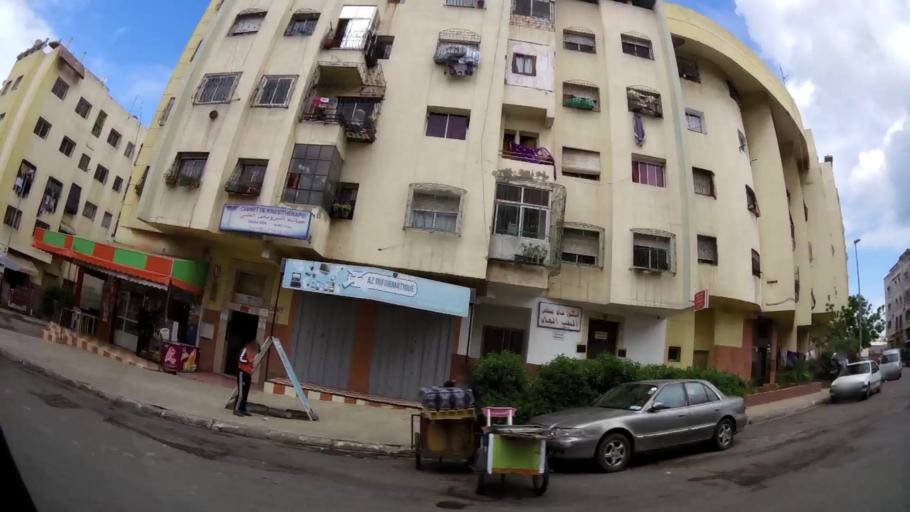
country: MA
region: Grand Casablanca
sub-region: Mediouna
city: Tit Mellil
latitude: 33.6001
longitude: -7.4899
